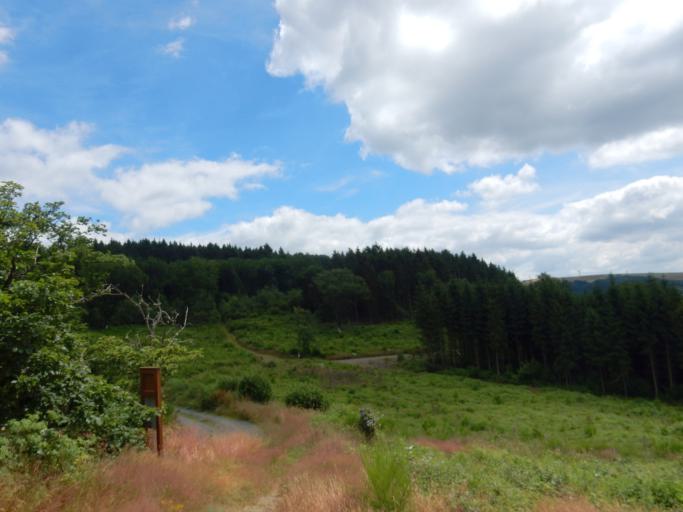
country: LU
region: Diekirch
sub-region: Canton de Diekirch
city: Bourscheid
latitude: 49.9452
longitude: 6.0293
